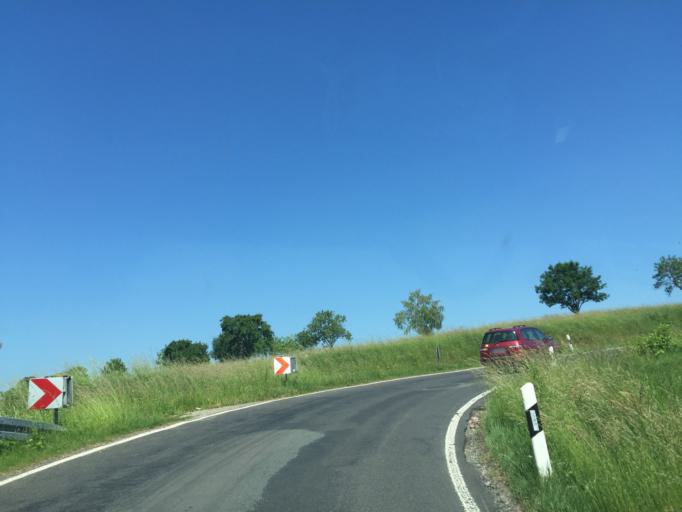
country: DE
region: Bavaria
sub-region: Regierungsbezirk Unterfranken
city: Weilbach
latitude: 49.6488
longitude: 9.2615
